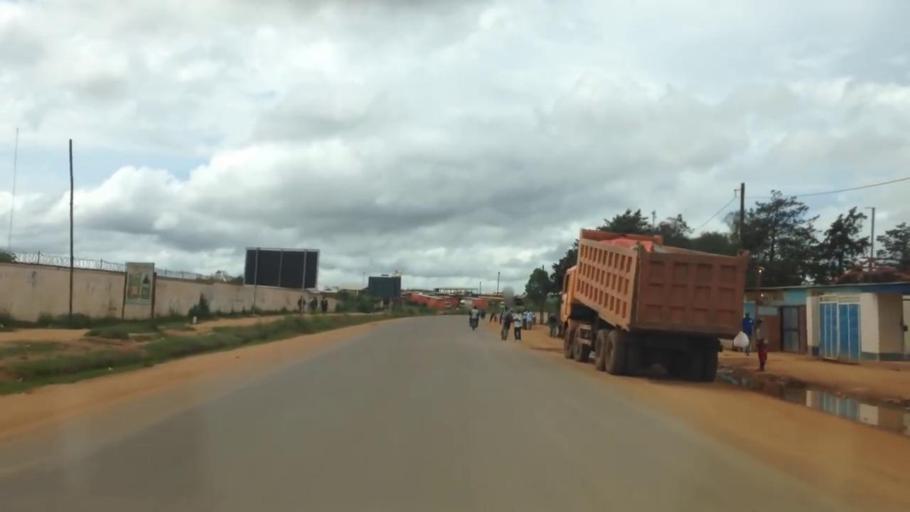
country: CD
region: Katanga
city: Kolwezi
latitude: -10.7221
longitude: 25.5072
